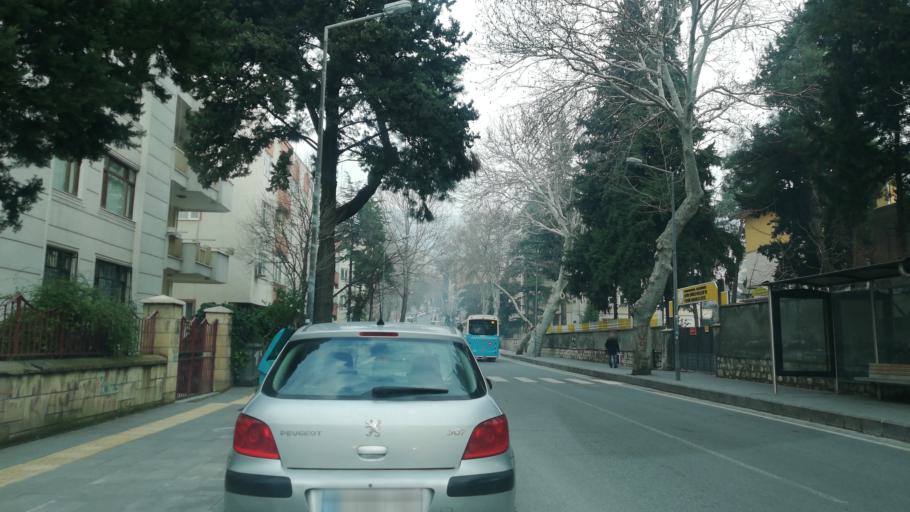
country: TR
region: Kahramanmaras
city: Kahramanmaras
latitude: 37.5884
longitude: 36.9303
